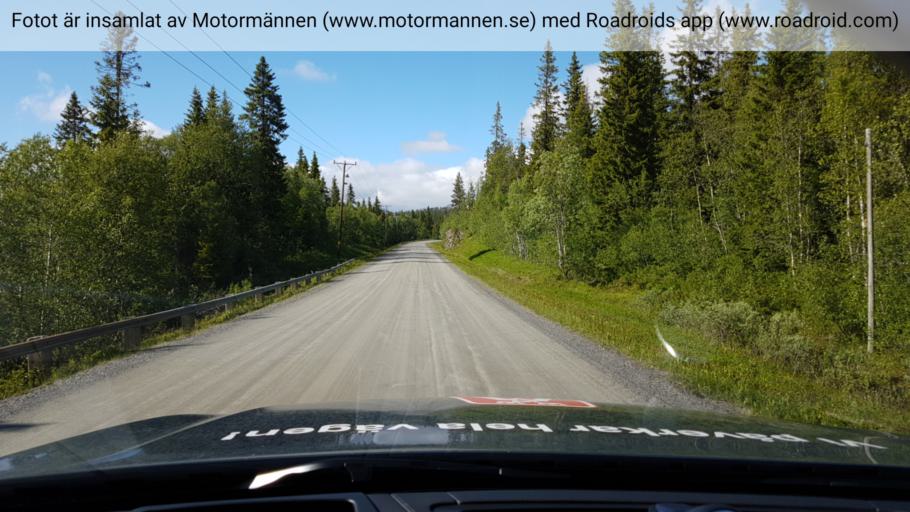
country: SE
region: Jaemtland
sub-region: Are Kommun
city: Are
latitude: 63.6823
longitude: 12.8096
